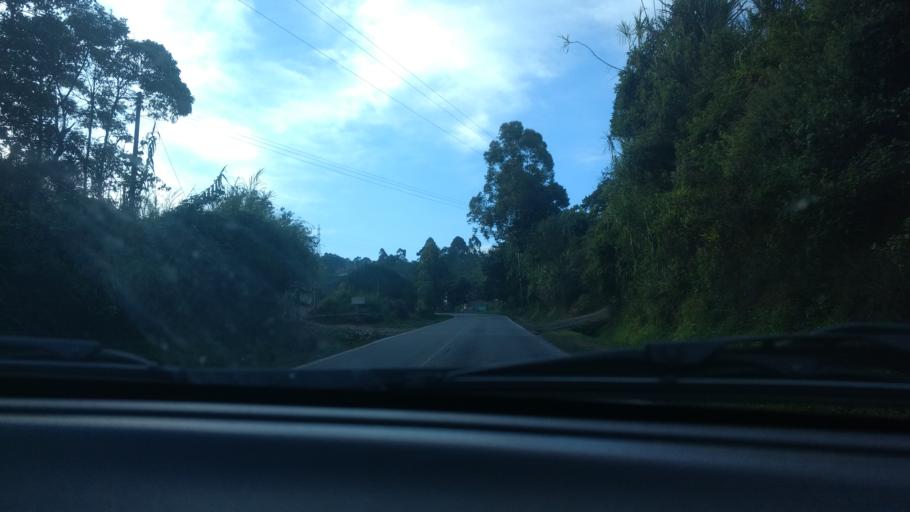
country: CO
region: Cauca
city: Rosas
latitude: 2.3385
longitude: -76.6944
